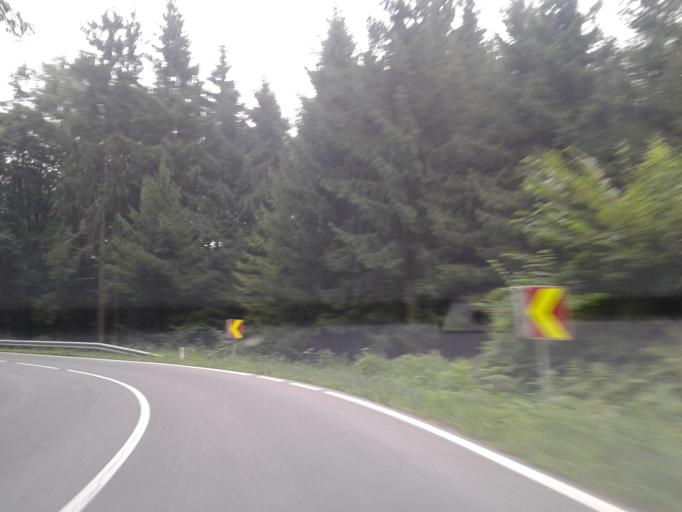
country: AT
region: Styria
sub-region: Politischer Bezirk Graz-Umgebung
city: Eggersdorf bei Graz
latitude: 47.1007
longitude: 15.5584
